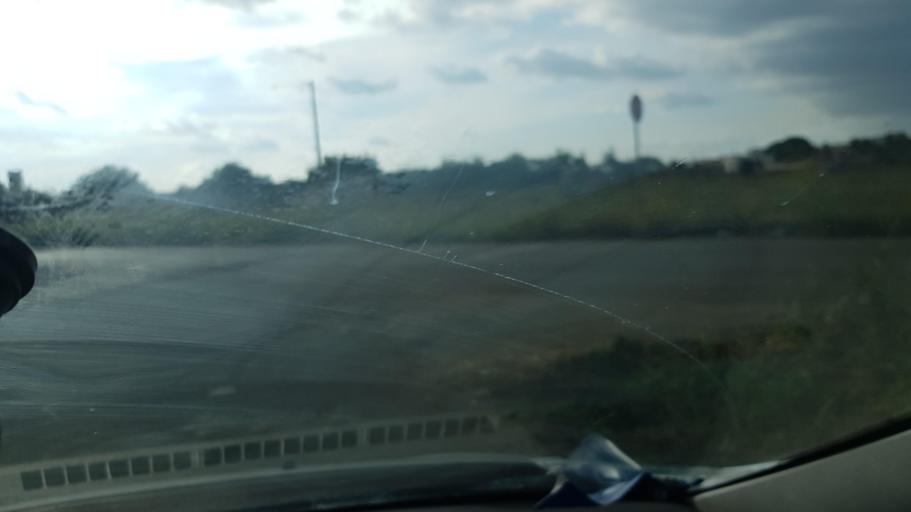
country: IT
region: Apulia
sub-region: Provincia di Brindisi
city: Cellino San Marco
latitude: 40.4654
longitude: 17.9638
